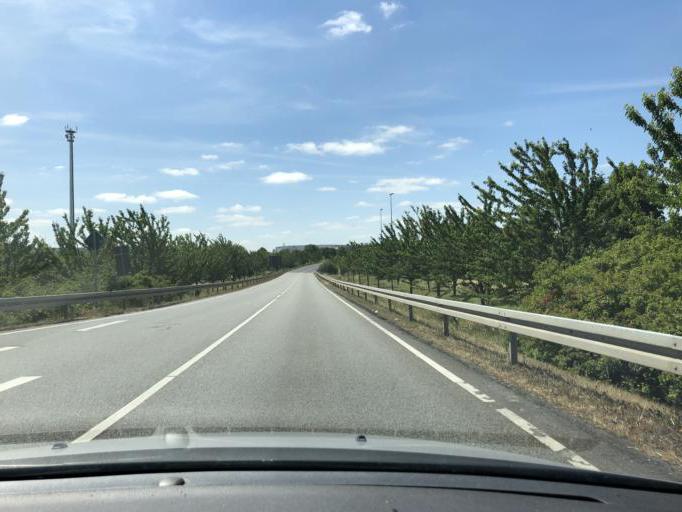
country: DE
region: Saxony-Anhalt
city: Osterfeld
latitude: 51.0919
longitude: 11.9525
